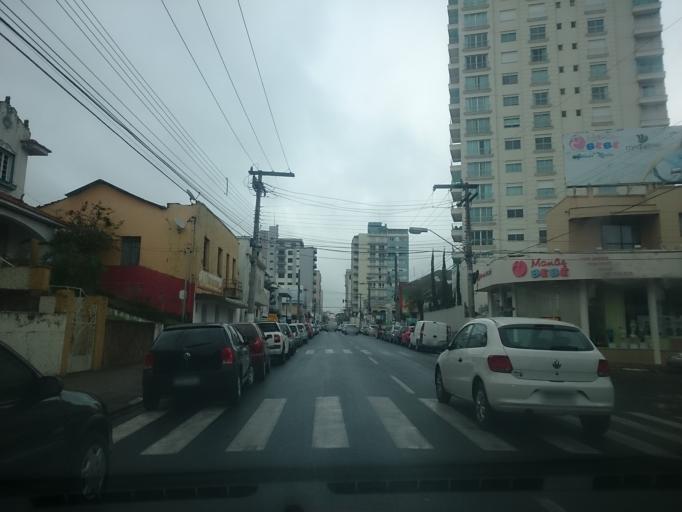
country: BR
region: Santa Catarina
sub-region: Lages
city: Lages
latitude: -27.8120
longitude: -50.3243
